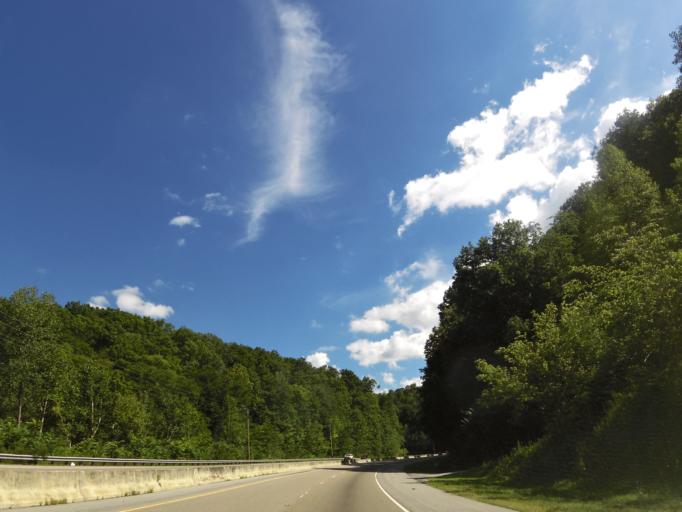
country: US
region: Tennessee
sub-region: Grainger County
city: Rutledge
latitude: 36.3718
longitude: -83.4389
